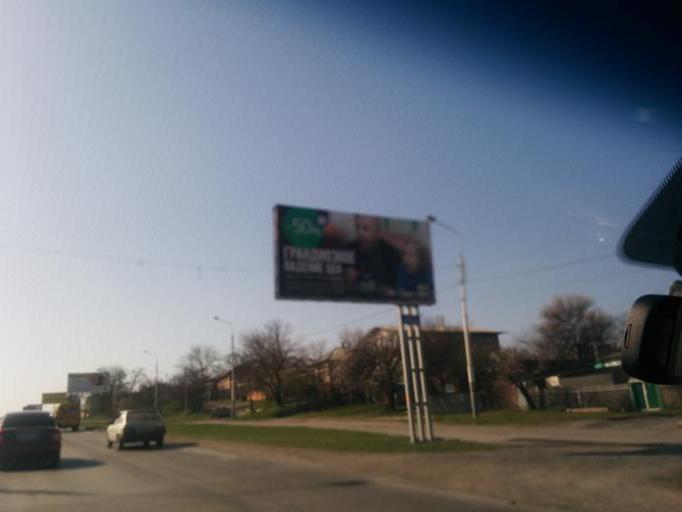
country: RU
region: Rostov
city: Shakhty
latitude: 47.7099
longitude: 40.1768
